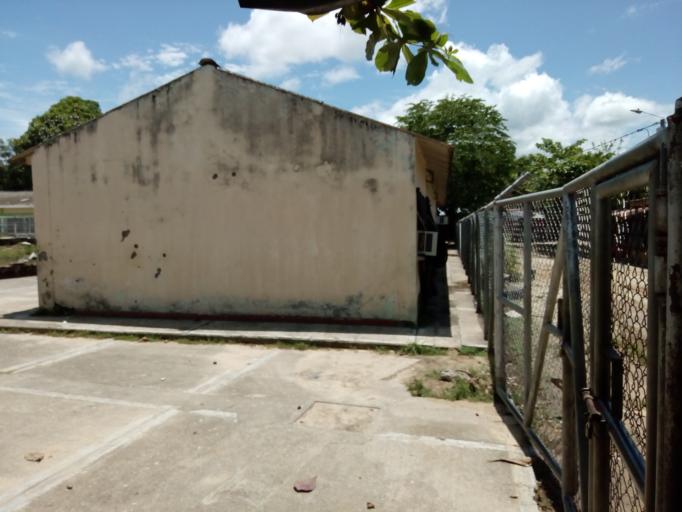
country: CO
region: Boyaca
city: Puerto Boyaca
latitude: 6.0672
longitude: -74.2682
